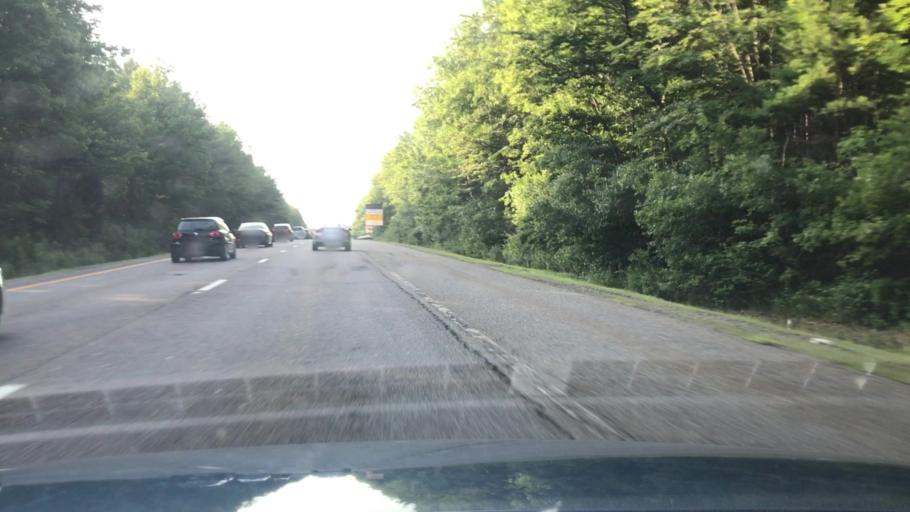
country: US
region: Massachusetts
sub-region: Plymouth County
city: Hanover
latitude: 42.1327
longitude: -70.8115
